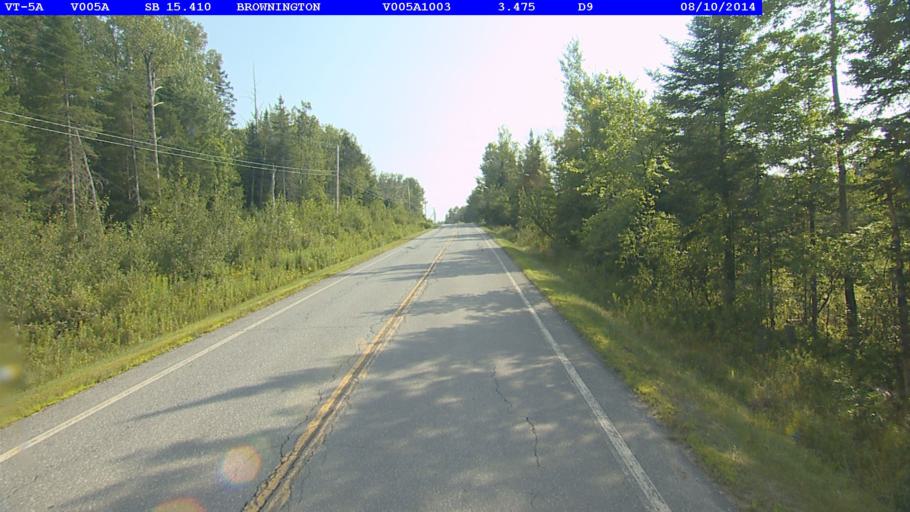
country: US
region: Vermont
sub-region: Orleans County
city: Newport
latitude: 44.8316
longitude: -72.0673
